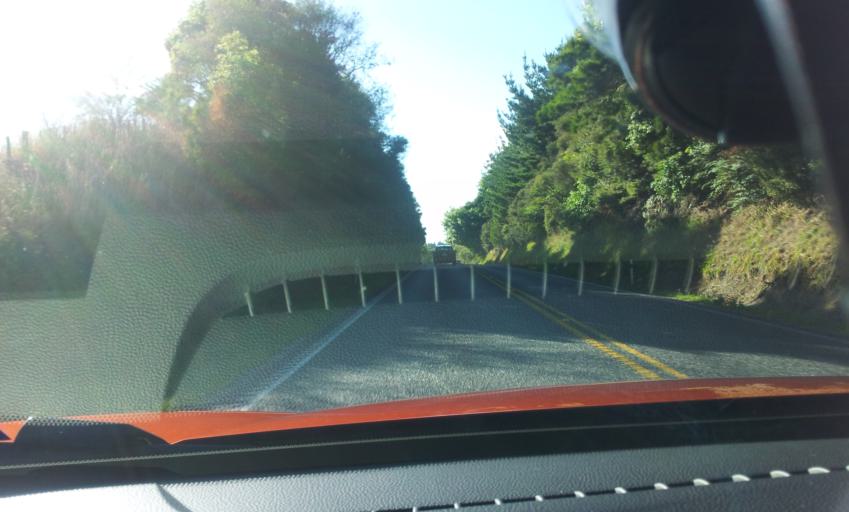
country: NZ
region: Waikato
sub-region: Hauraki District
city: Ngatea
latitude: -37.2780
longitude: 175.3480
